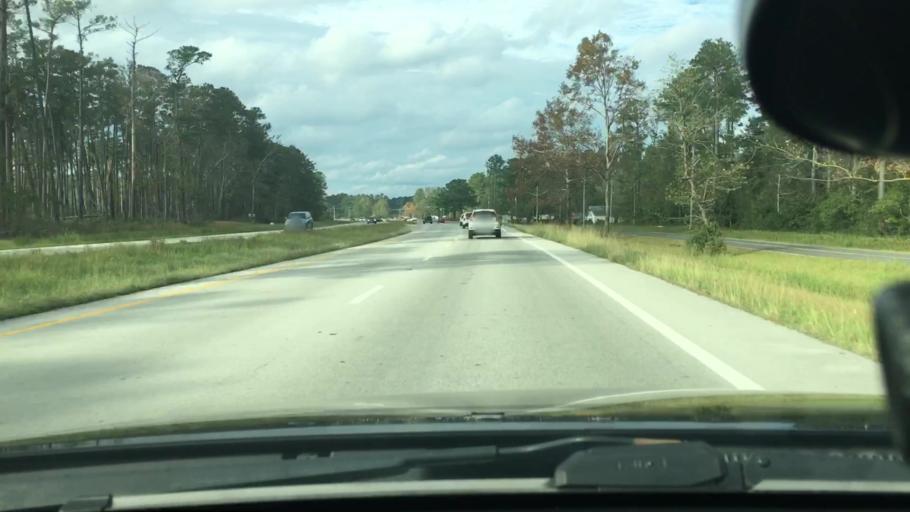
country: US
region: North Carolina
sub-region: Craven County
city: Neuse Forest
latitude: 34.9459
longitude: -76.9483
